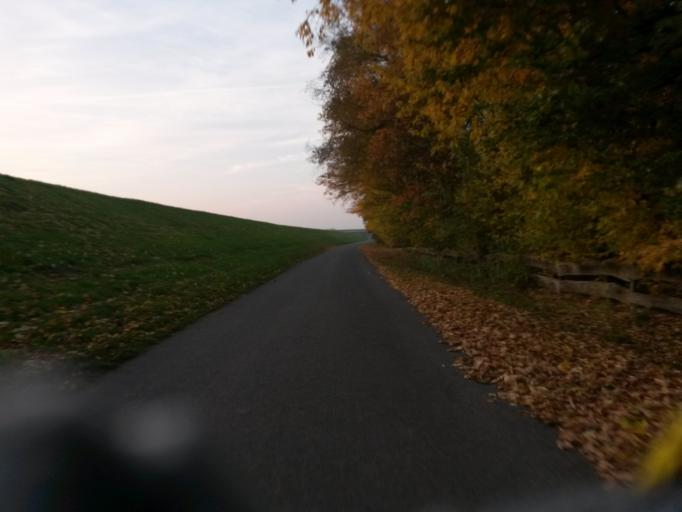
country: DE
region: Bremen
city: Bremen
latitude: 53.0326
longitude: 8.8756
